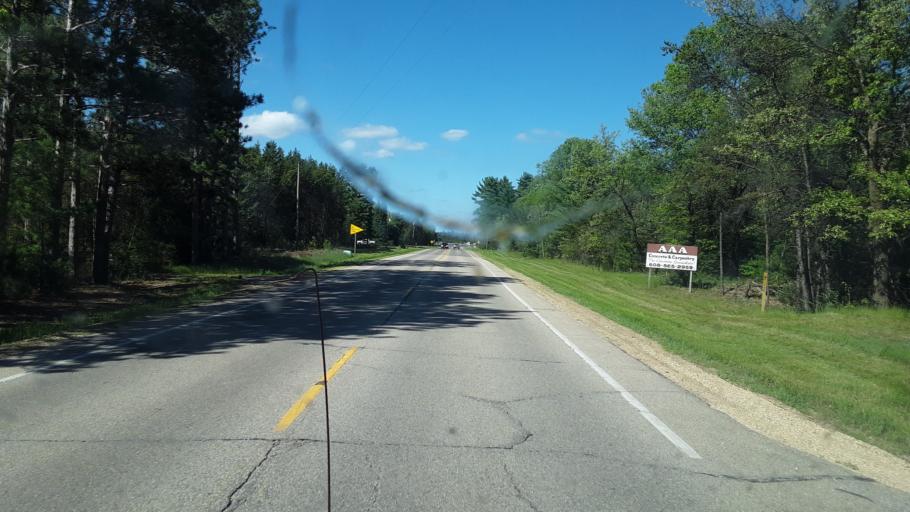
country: US
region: Wisconsin
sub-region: Juneau County
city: New Lisbon
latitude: 43.9664
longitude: -90.0763
